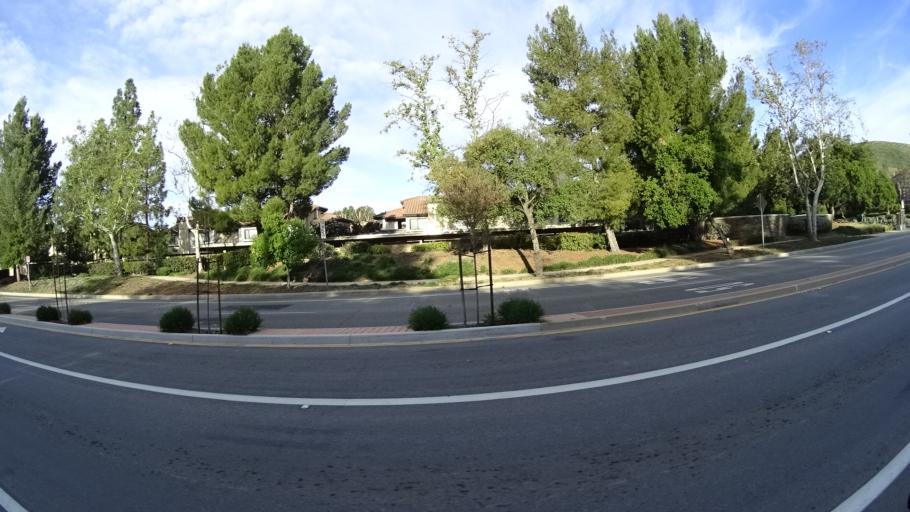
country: US
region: California
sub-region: Ventura County
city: Thousand Oaks
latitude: 34.2136
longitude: -118.8230
